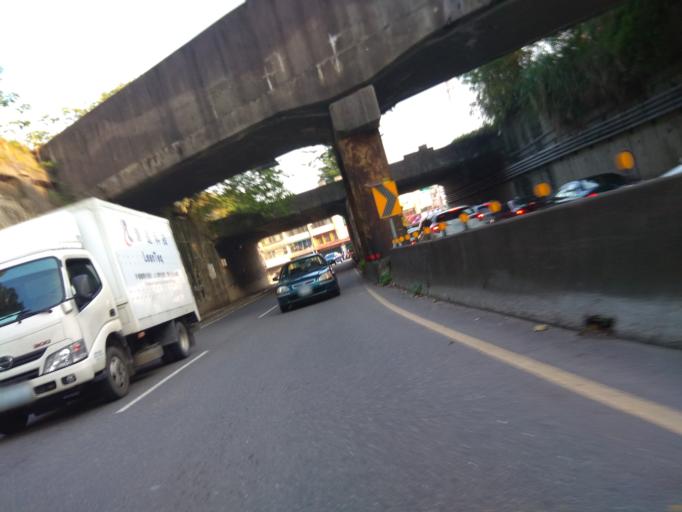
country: TW
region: Taiwan
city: Daxi
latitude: 24.9240
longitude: 121.1871
